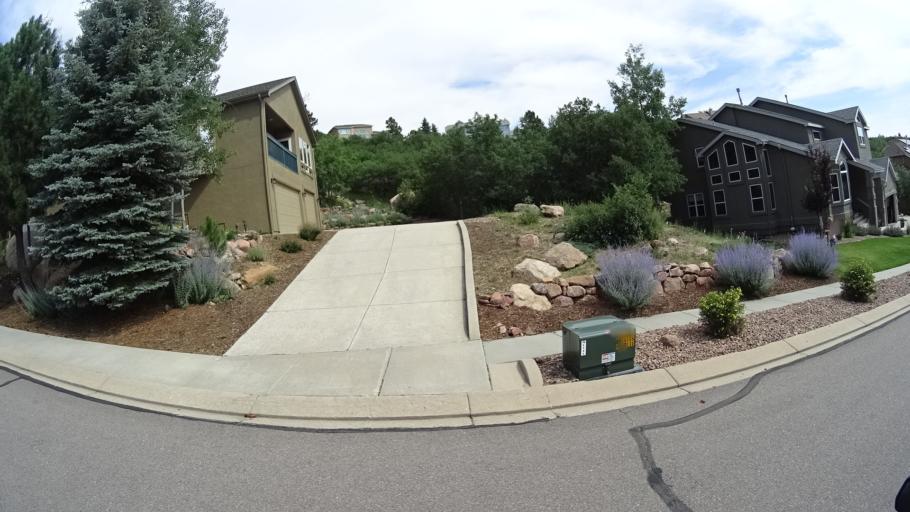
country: US
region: Colorado
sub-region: El Paso County
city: Air Force Academy
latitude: 38.9522
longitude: -104.8885
